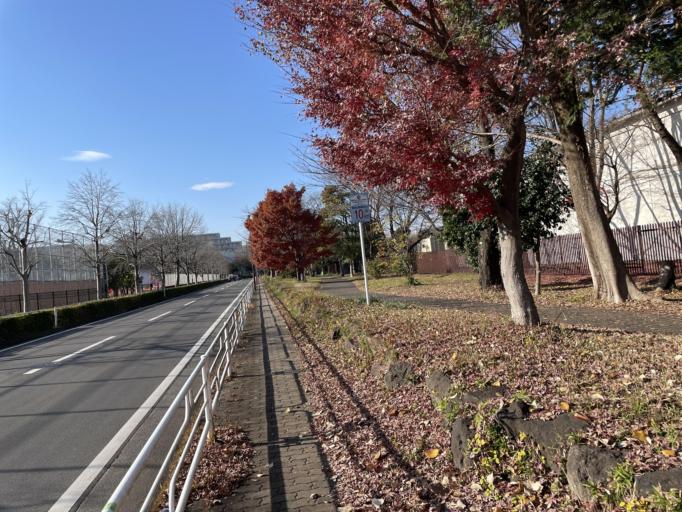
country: JP
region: Saitama
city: Asaka
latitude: 35.7783
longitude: 139.5905
